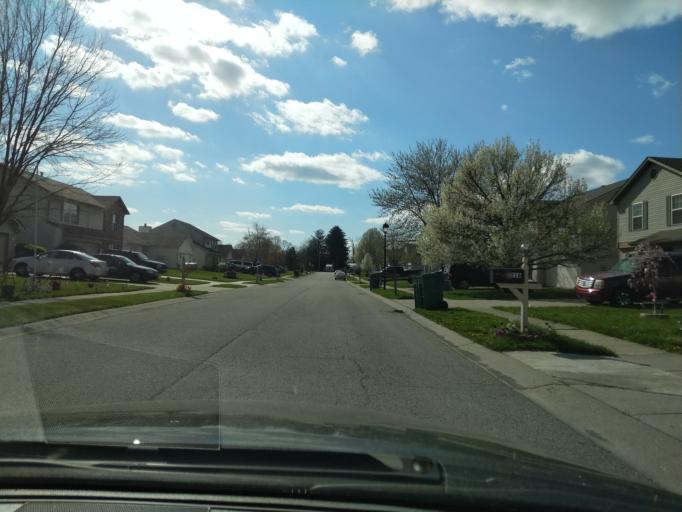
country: US
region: Indiana
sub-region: Boone County
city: Zionsville
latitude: 39.8871
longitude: -86.2339
